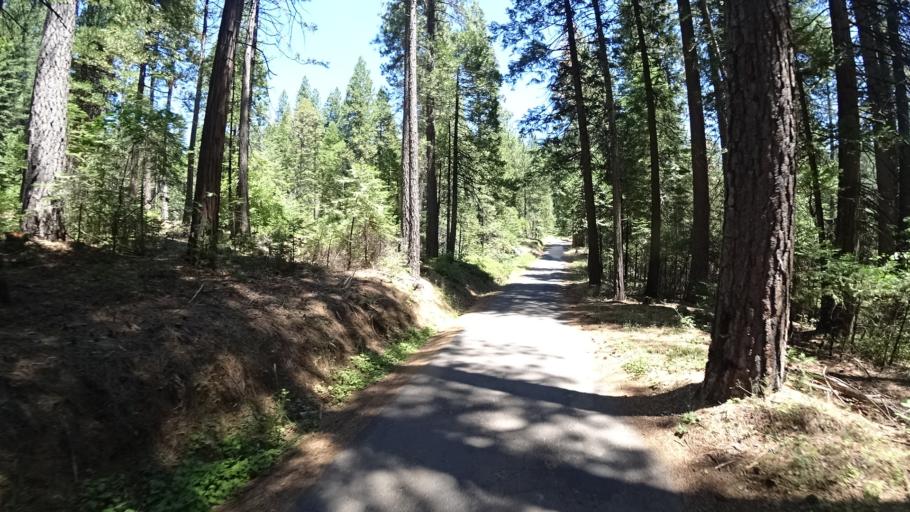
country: US
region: California
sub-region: Calaveras County
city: Arnold
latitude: 38.2367
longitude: -120.3204
